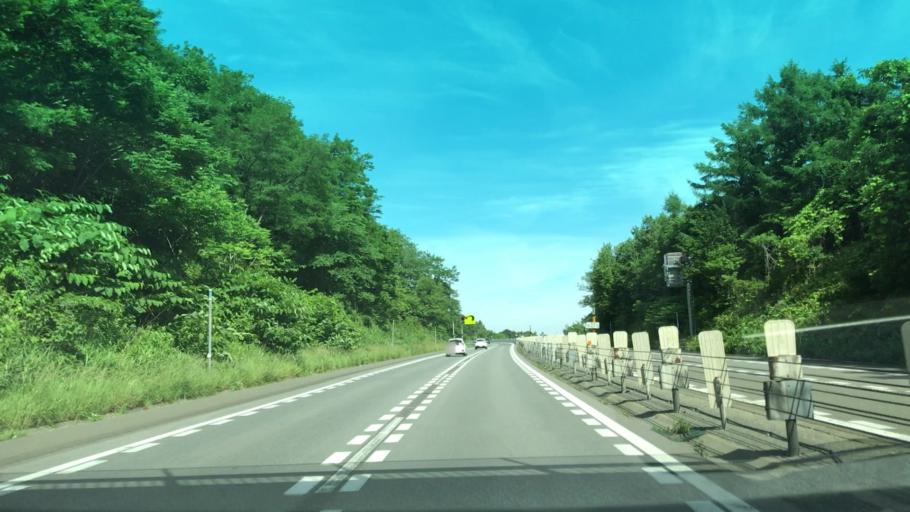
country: JP
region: Hokkaido
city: Otaru
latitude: 43.1487
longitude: 141.1303
